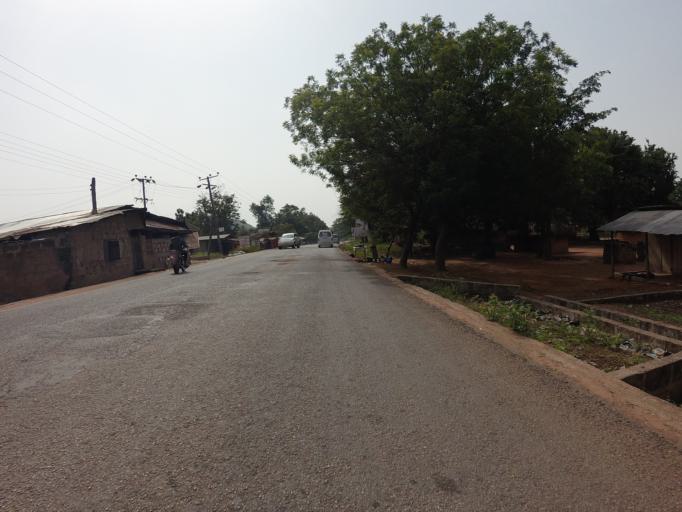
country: GH
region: Volta
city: Ho
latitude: 6.3773
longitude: 0.1882
